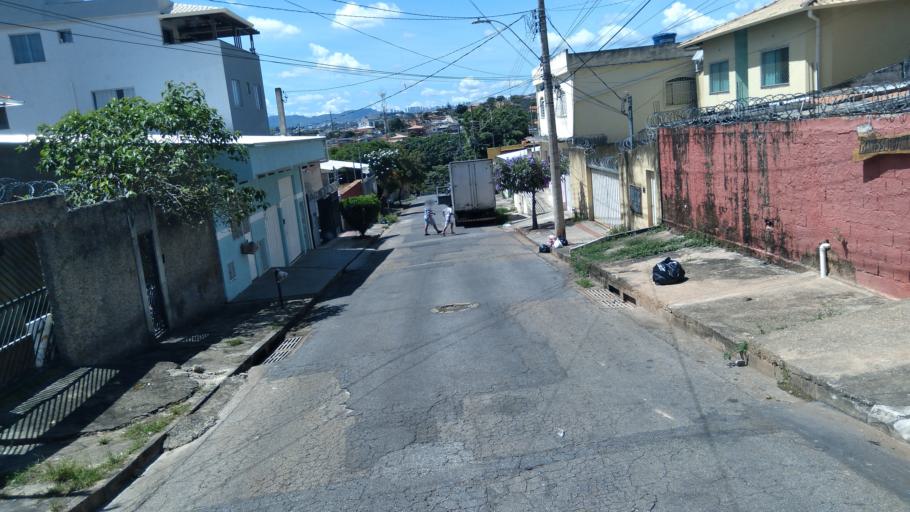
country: BR
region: Minas Gerais
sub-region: Contagem
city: Contagem
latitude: -19.8956
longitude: -44.0180
